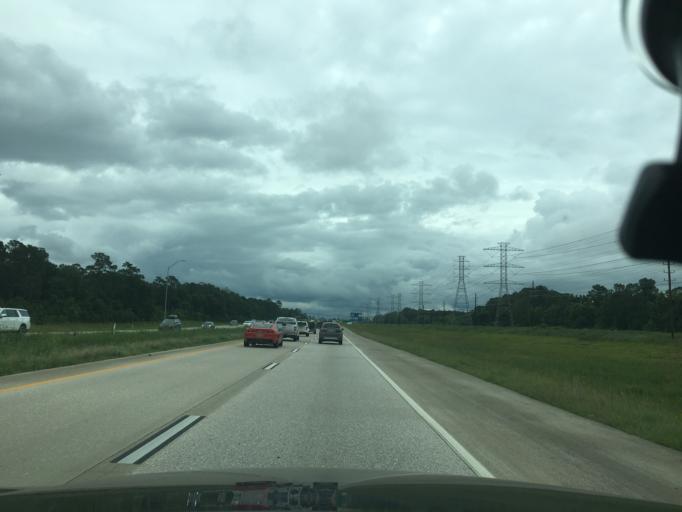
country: US
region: Texas
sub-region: Harris County
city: Spring
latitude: 30.0912
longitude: -95.4704
